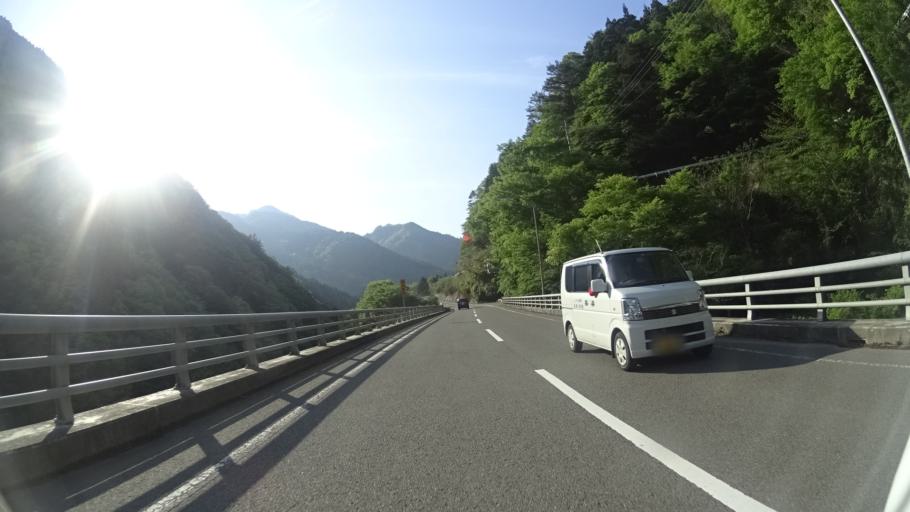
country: JP
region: Tokushima
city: Ikedacho
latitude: 33.8619
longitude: 133.8780
